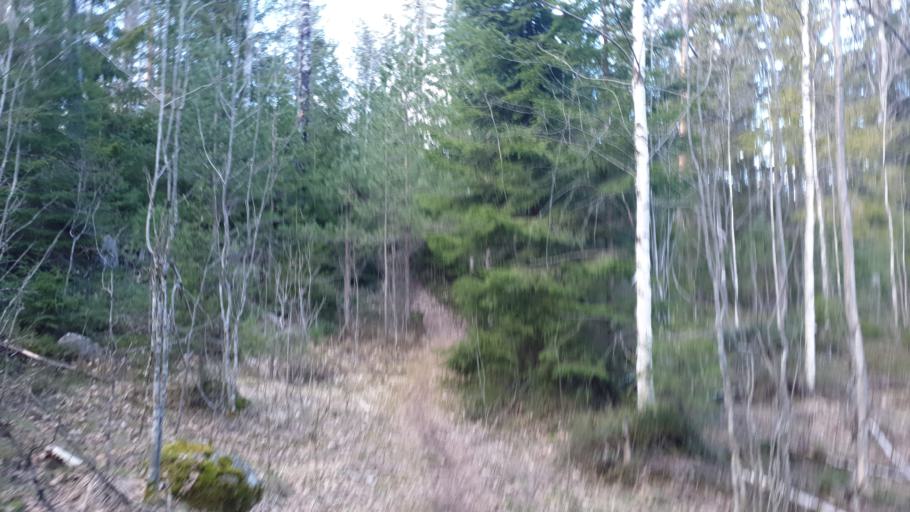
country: SE
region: OErebro
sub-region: Orebro Kommun
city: Garphyttan
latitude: 59.3693
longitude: 14.9738
